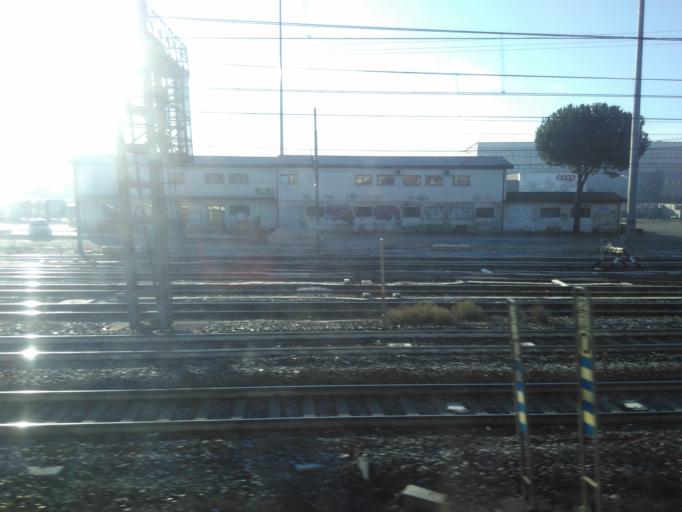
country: IT
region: Veneto
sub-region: Provincia di Padova
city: Padova
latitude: 45.4175
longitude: 11.8875
